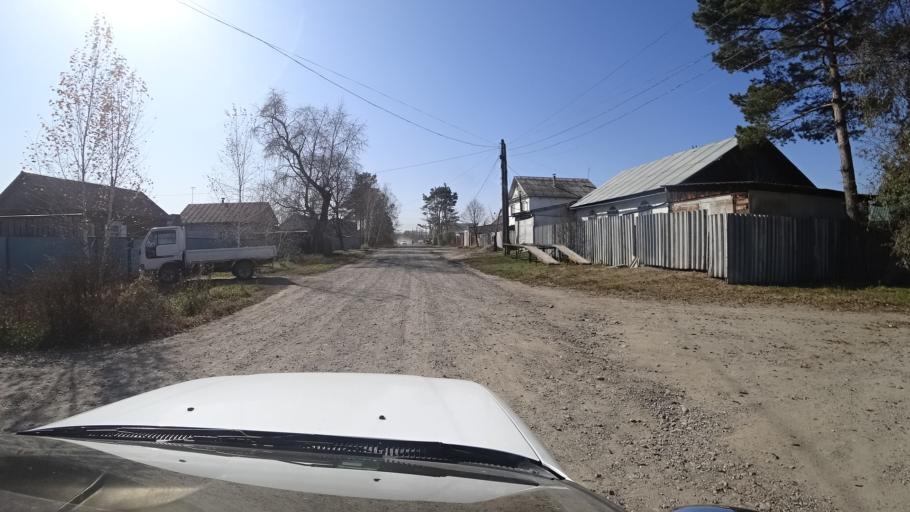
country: RU
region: Primorskiy
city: Dal'nerechensk
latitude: 45.9278
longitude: 133.7460
